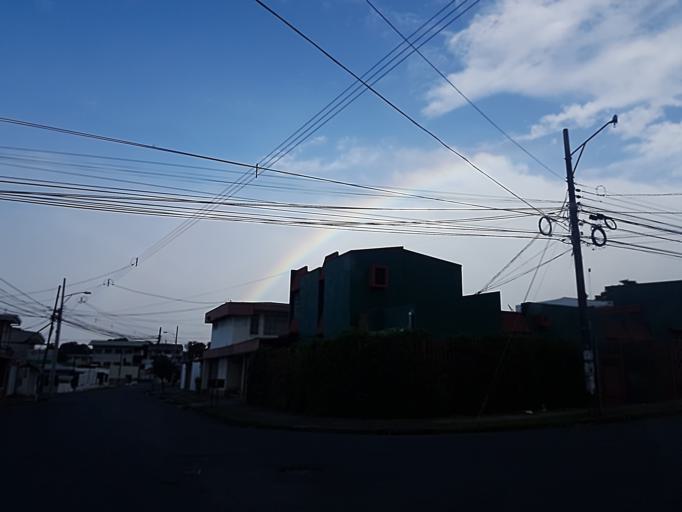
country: CR
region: San Jose
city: San Pedro
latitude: 9.9281
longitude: -84.0487
